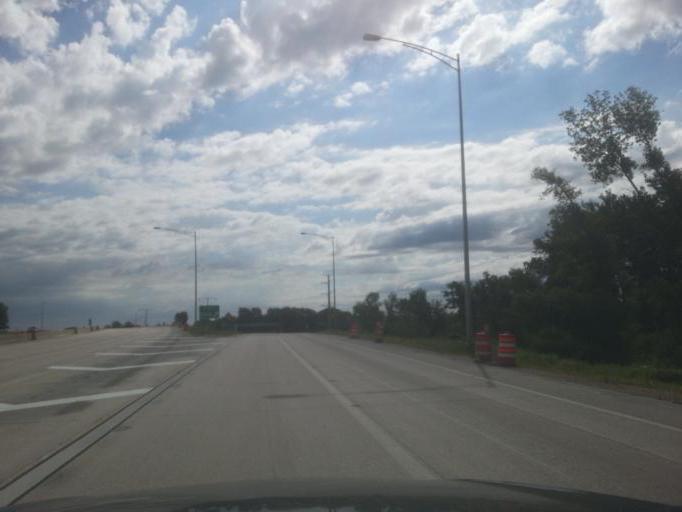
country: US
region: Wisconsin
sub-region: Dane County
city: Monona
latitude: 43.0452
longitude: -89.3113
